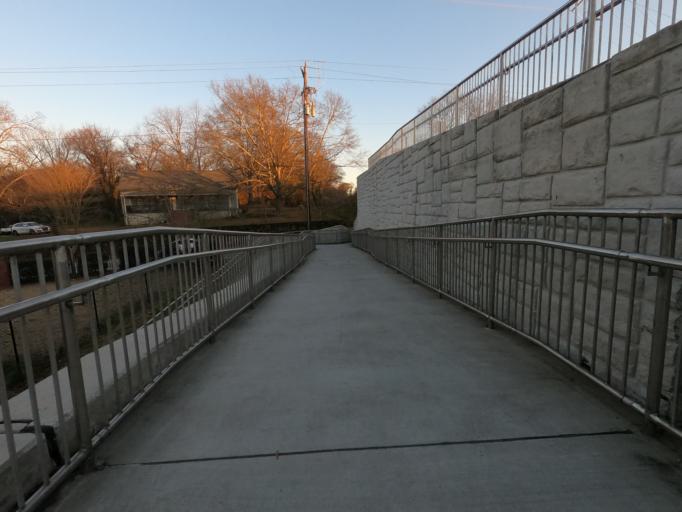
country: US
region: Georgia
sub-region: Clarke County
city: Athens
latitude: 33.9541
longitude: -83.3640
